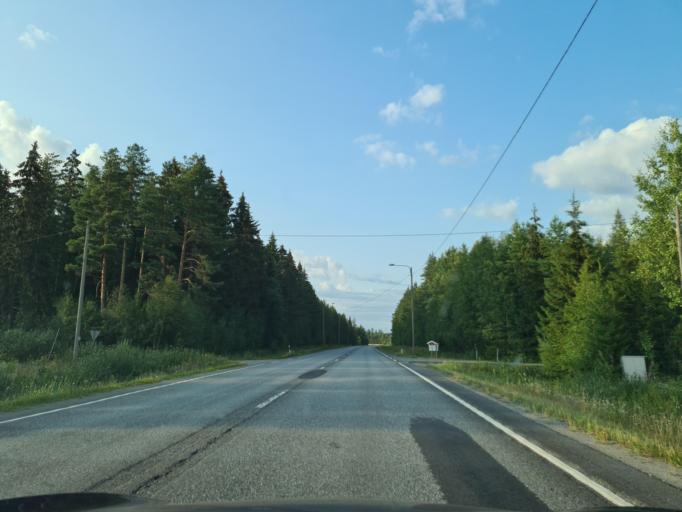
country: FI
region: Southern Ostrobothnia
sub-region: Seinaejoki
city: Kauhava
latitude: 63.0643
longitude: 23.0434
